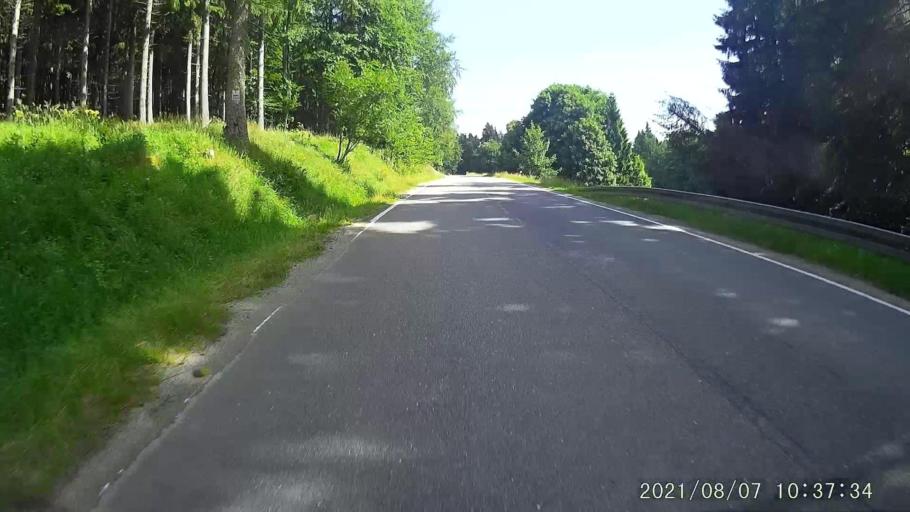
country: PL
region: Lower Silesian Voivodeship
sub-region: Powiat klodzki
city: Duszniki-Zdroj
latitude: 50.3549
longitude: 16.3725
